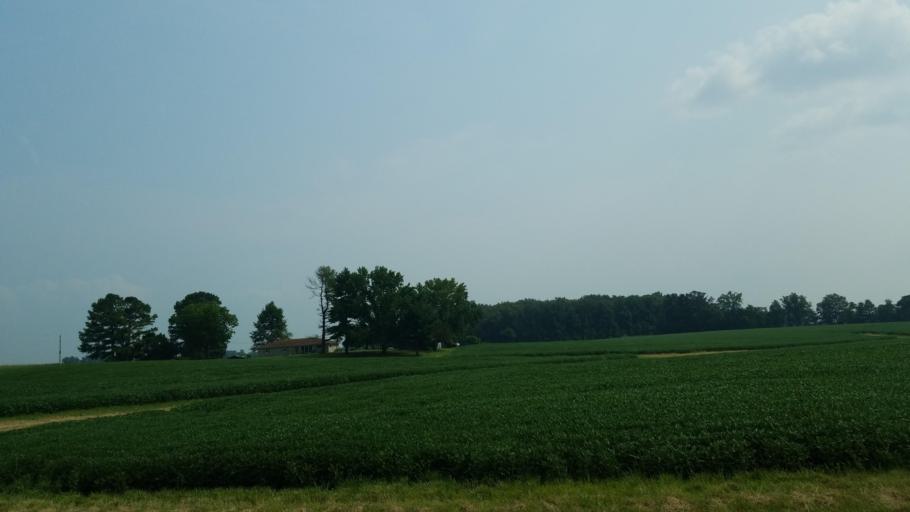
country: US
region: Illinois
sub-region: Saline County
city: Harrisburg
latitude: 37.8353
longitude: -88.5504
